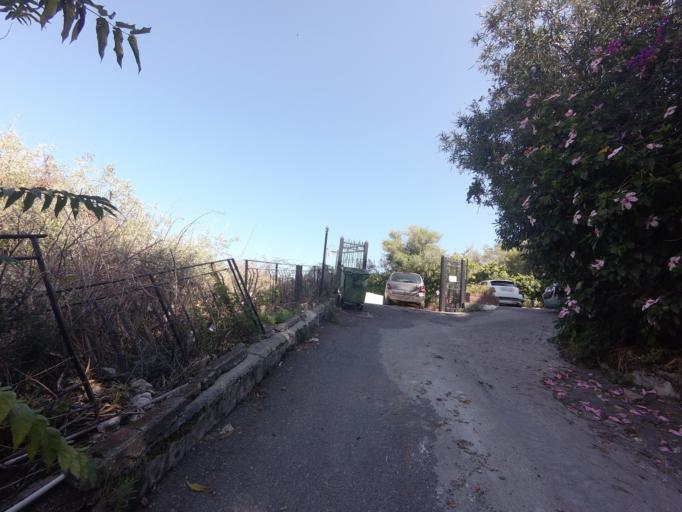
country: IT
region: Sicily
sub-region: Messina
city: Taormina
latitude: 37.8546
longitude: 15.2999
